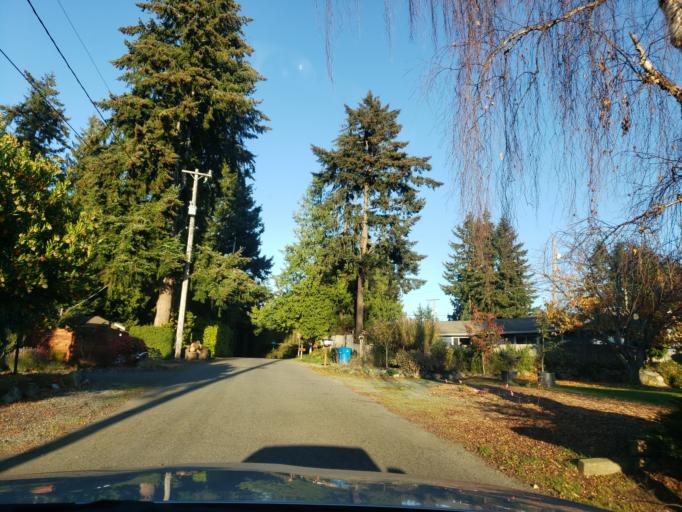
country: US
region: Washington
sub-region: Snohomish County
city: Woodway
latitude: 47.7774
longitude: -122.3837
